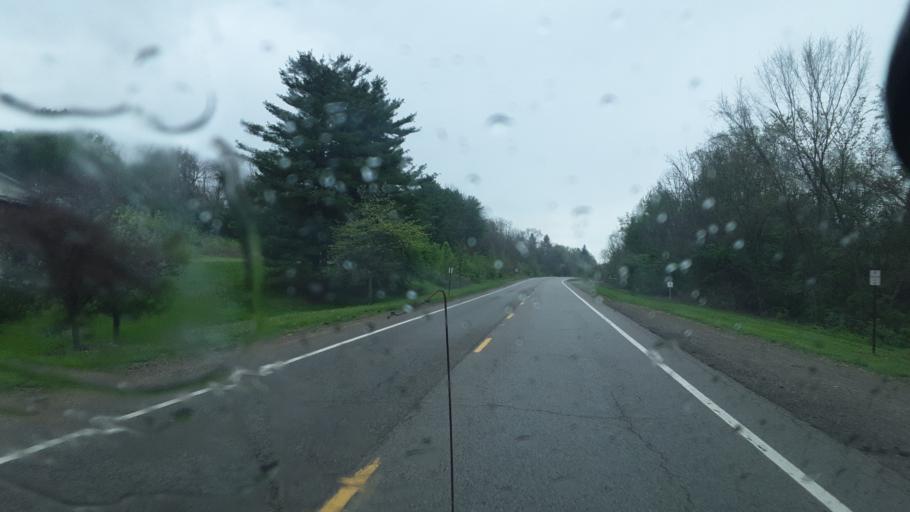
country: US
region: Ohio
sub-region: Muskingum County
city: New Concord
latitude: 39.9863
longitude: -81.7362
